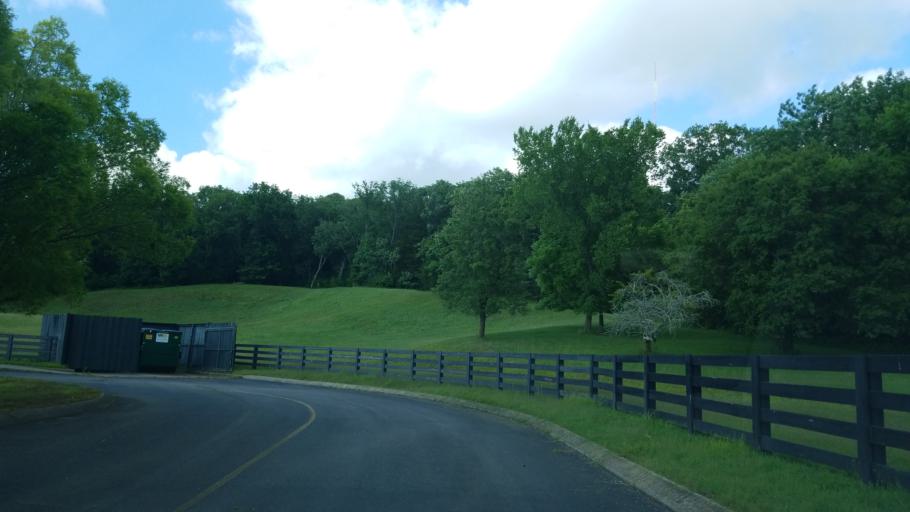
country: US
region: Tennessee
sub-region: Davidson County
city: Forest Hills
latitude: 36.0300
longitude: -86.8569
